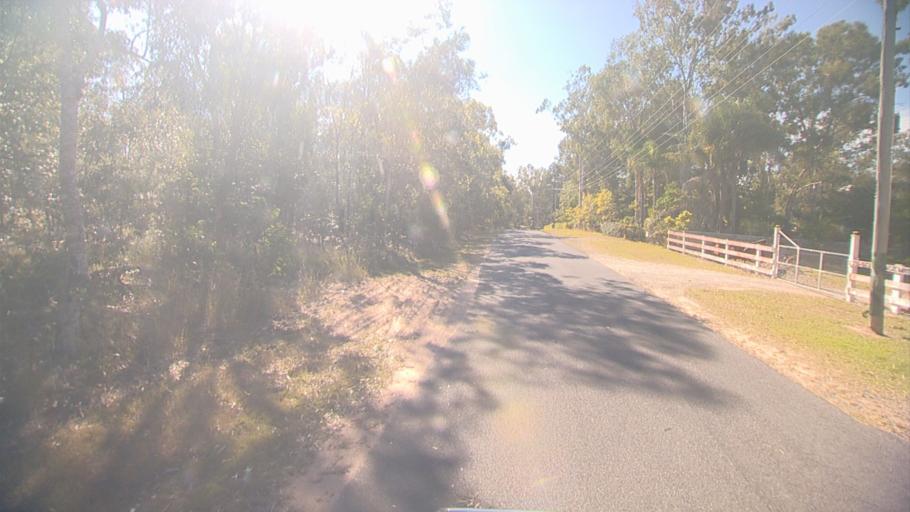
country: AU
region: Queensland
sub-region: Ipswich
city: Springfield Lakes
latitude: -27.7191
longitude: 152.9551
